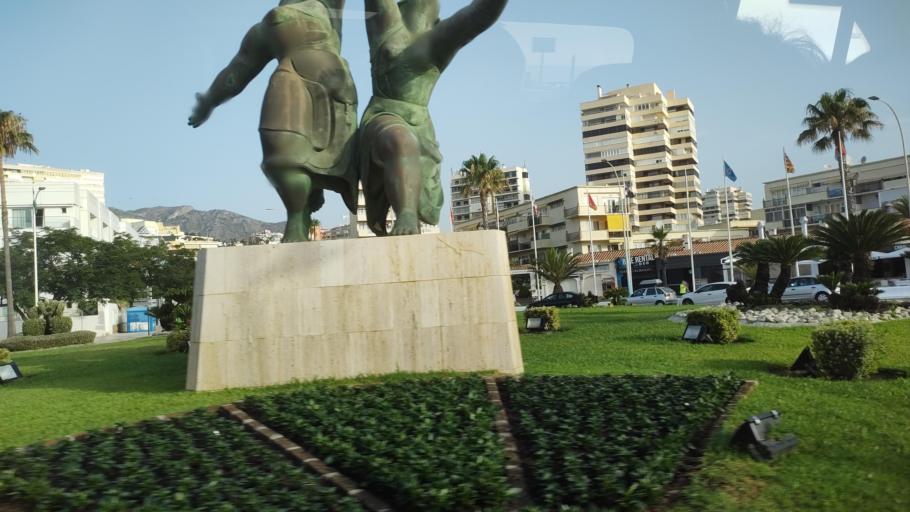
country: ES
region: Andalusia
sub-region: Provincia de Malaga
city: Torremolinos
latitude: 36.6267
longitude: -4.4920
